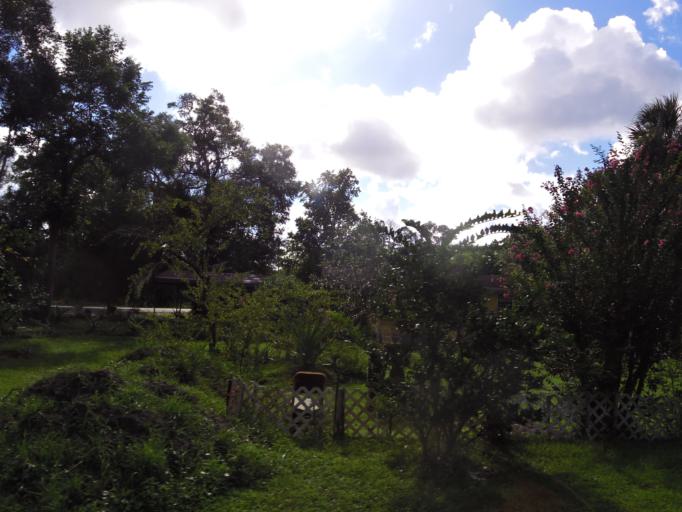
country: US
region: Georgia
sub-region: Camden County
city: Kingsland
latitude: 30.8040
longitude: -81.6946
